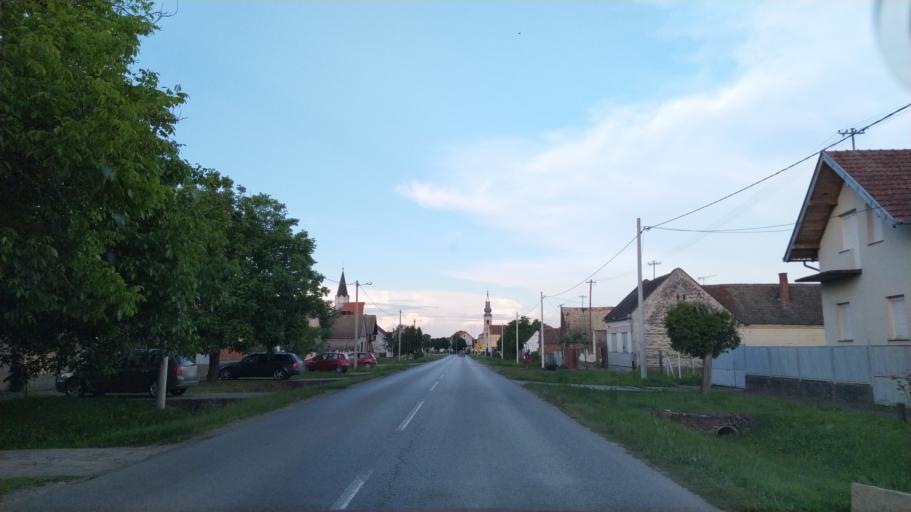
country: HR
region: Osjecko-Baranjska
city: Gorjani
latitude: 45.4610
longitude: 18.3190
